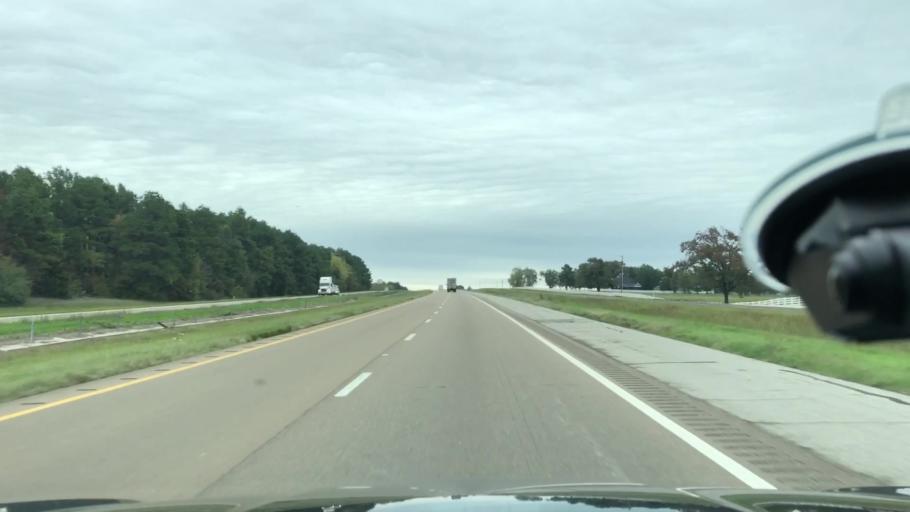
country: US
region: Texas
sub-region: Titus County
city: Mount Pleasant
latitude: 33.2051
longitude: -94.9077
